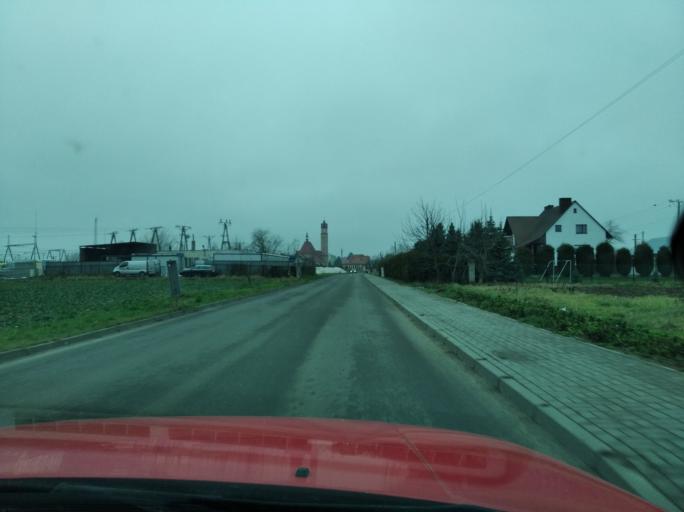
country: PL
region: Subcarpathian Voivodeship
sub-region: Powiat przeworski
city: Przeworsk
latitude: 50.0602
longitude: 22.5143
